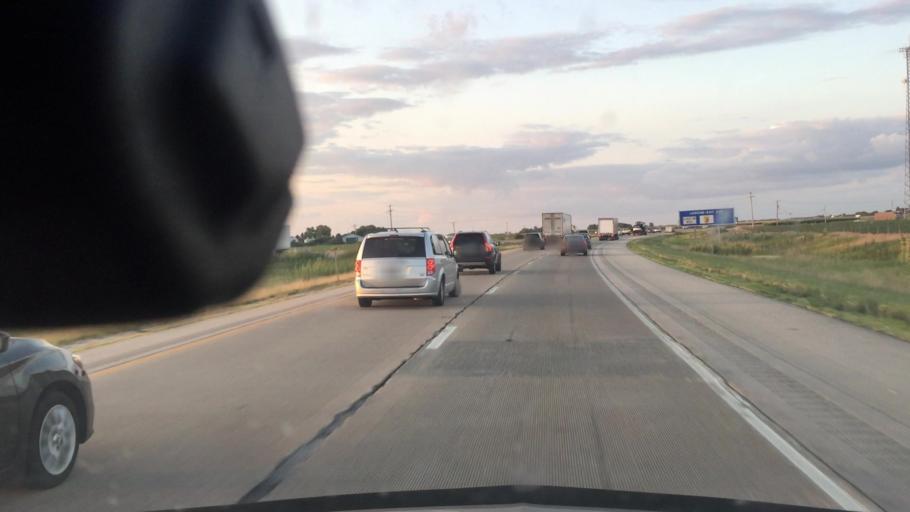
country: US
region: Illinois
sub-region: Livingston County
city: Dwight
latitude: 41.1071
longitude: -88.4474
